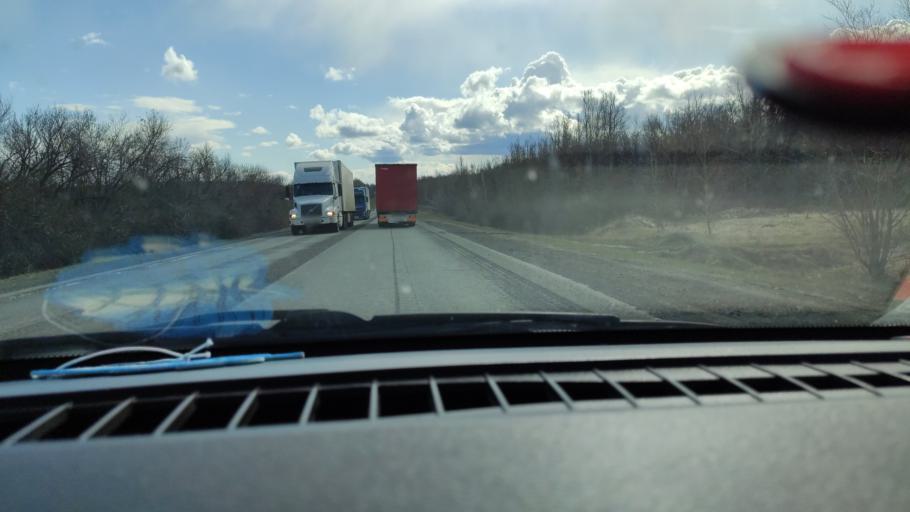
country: RU
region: Saratov
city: Dukhovnitskoye
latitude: 52.6286
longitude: 48.1821
